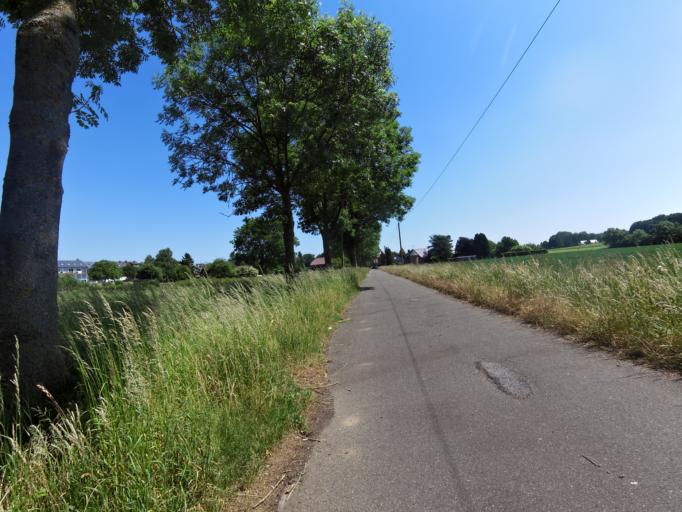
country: DE
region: North Rhine-Westphalia
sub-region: Regierungsbezirk Koln
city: Gangelt
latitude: 50.9814
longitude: 6.0564
